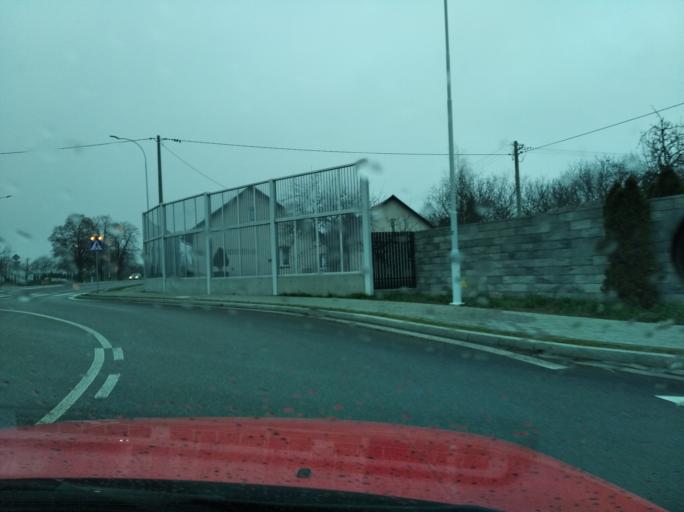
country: PL
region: Subcarpathian Voivodeship
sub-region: Powiat przeworski
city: Grzeska
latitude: 50.0617
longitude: 22.4677
